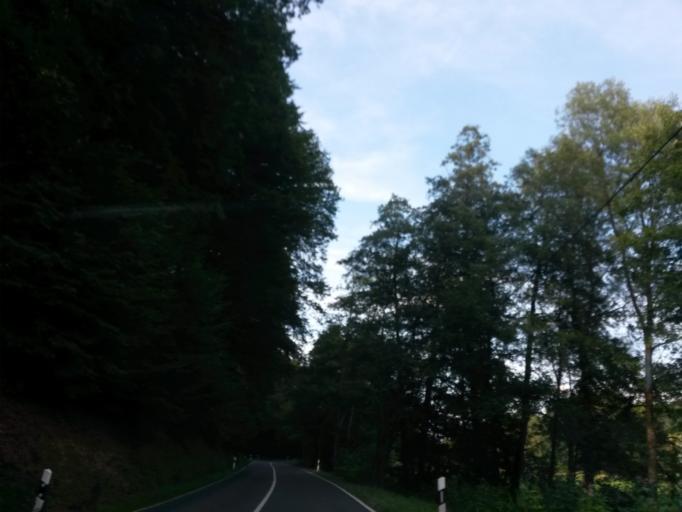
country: DE
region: North Rhine-Westphalia
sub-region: Regierungsbezirk Koln
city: Lindlar
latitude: 50.9985
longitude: 7.3394
